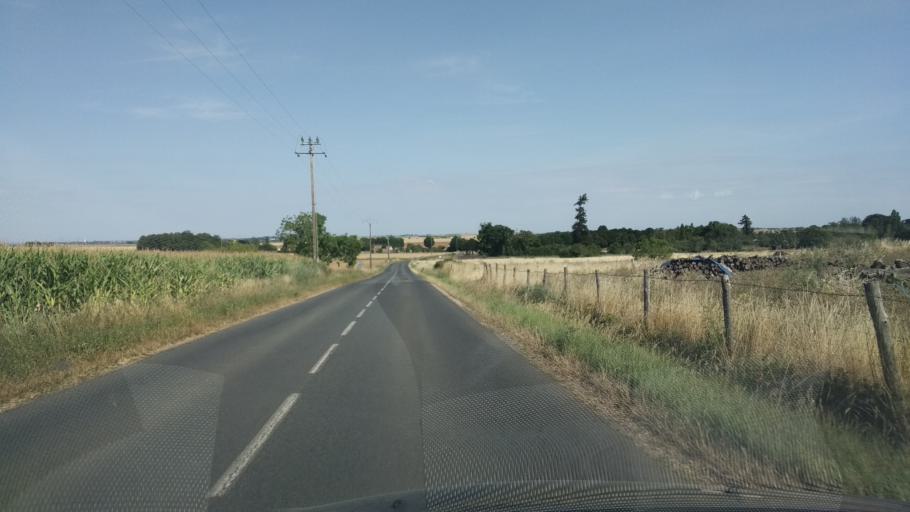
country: FR
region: Poitou-Charentes
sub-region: Departement de la Vienne
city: Vouille
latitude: 46.6819
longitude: 0.1714
